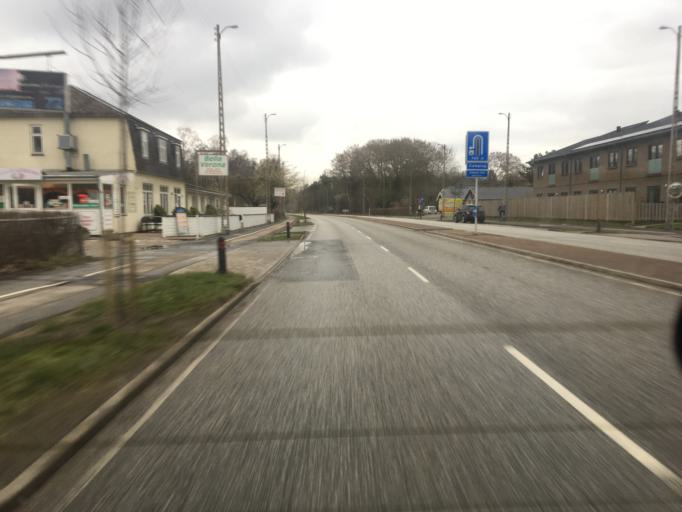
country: DK
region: Capital Region
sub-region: Ishoj Kommune
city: Ishoj
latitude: 55.5939
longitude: 12.3426
